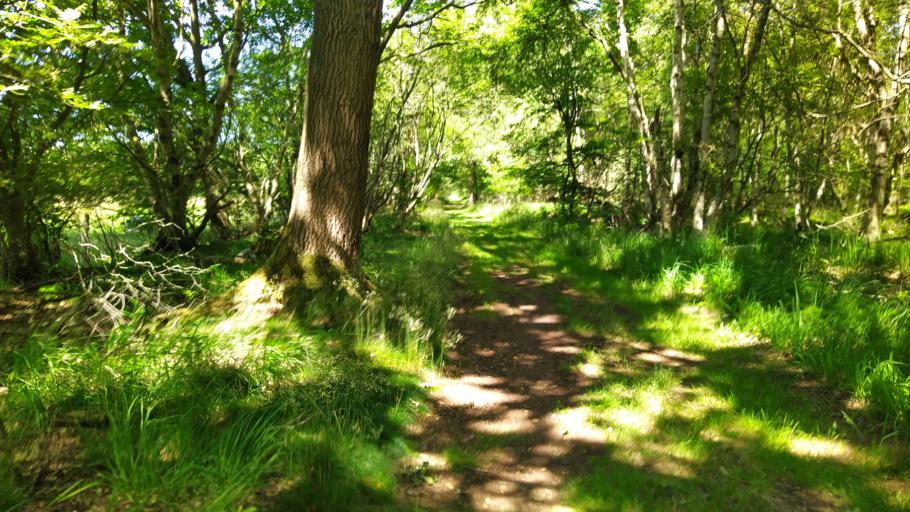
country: DE
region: Lower Saxony
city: Oldendorf
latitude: 53.5607
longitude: 9.2544
